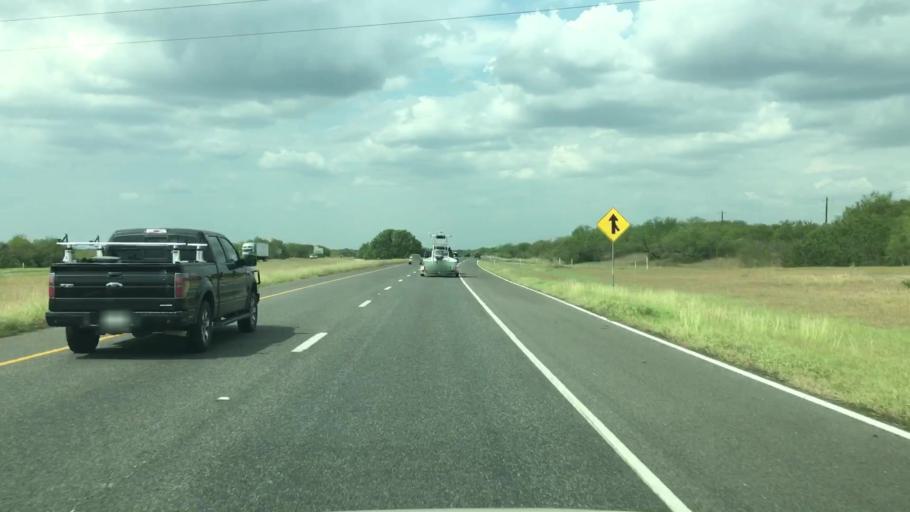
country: US
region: Texas
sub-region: Atascosa County
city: Pleasanton
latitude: 28.9174
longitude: -98.4347
